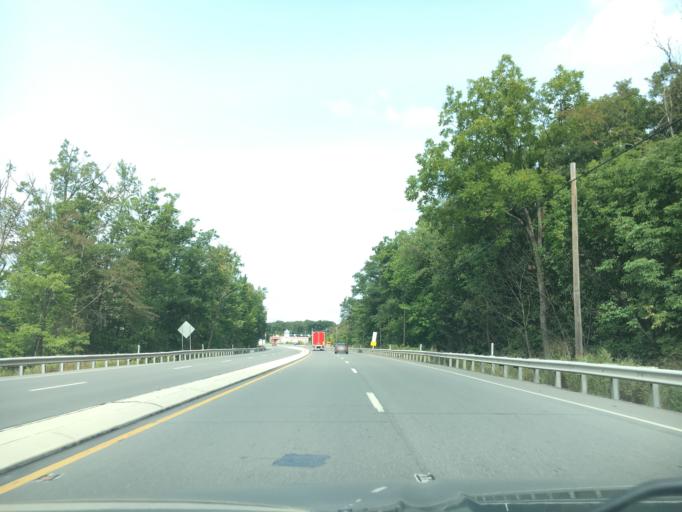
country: US
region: Pennsylvania
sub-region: Schuylkill County
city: Hometown
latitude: 40.8308
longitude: -75.9865
